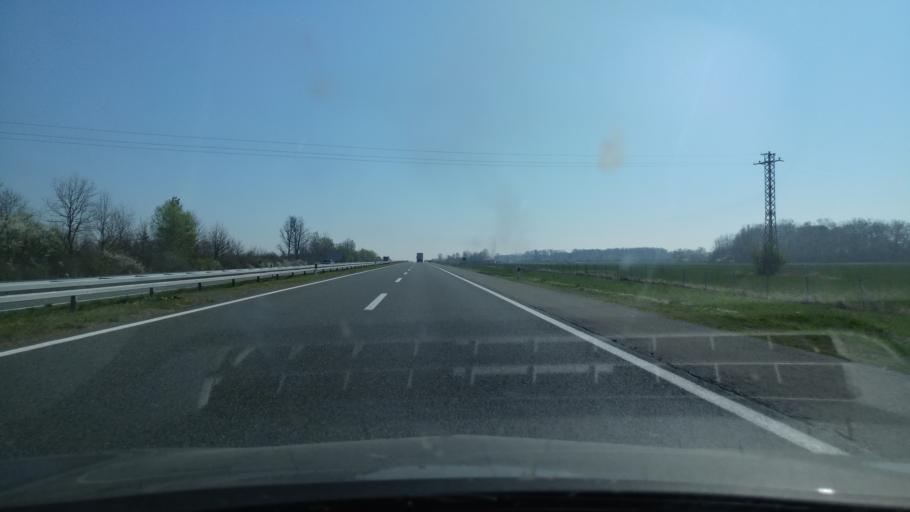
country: HR
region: Brodsko-Posavska
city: Bukovlje
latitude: 45.1746
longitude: 18.0979
